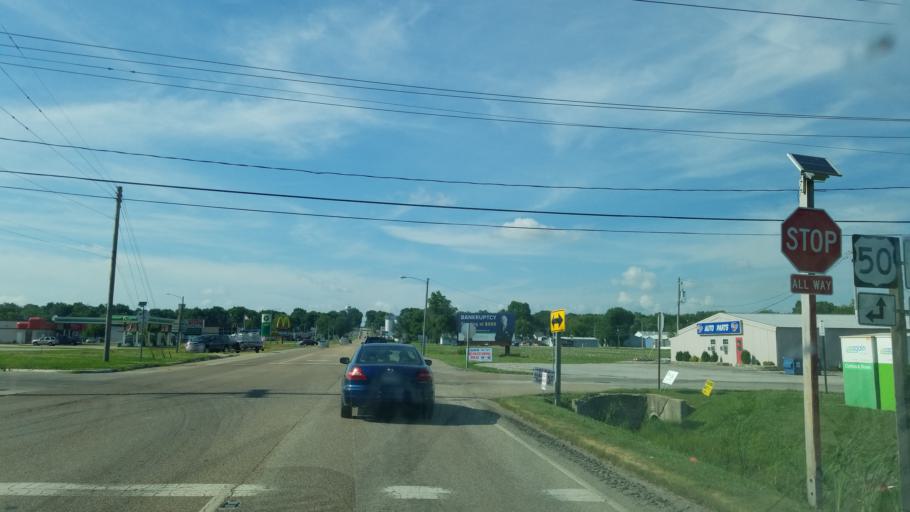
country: US
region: Illinois
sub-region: Saint Clair County
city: Lebanon
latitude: 38.5947
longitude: -89.8077
